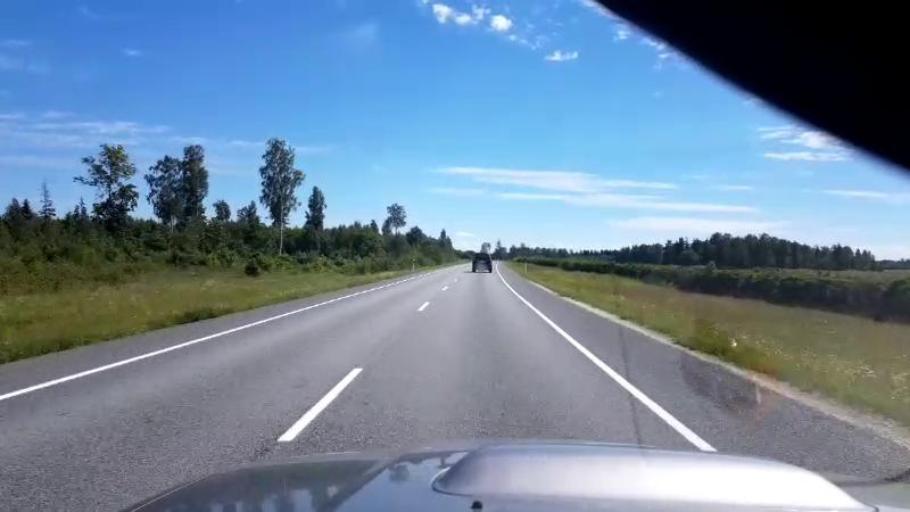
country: EE
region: Jaervamaa
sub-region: Jaerva-Jaani vald
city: Jarva-Jaani
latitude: 59.0222
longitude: 25.9003
